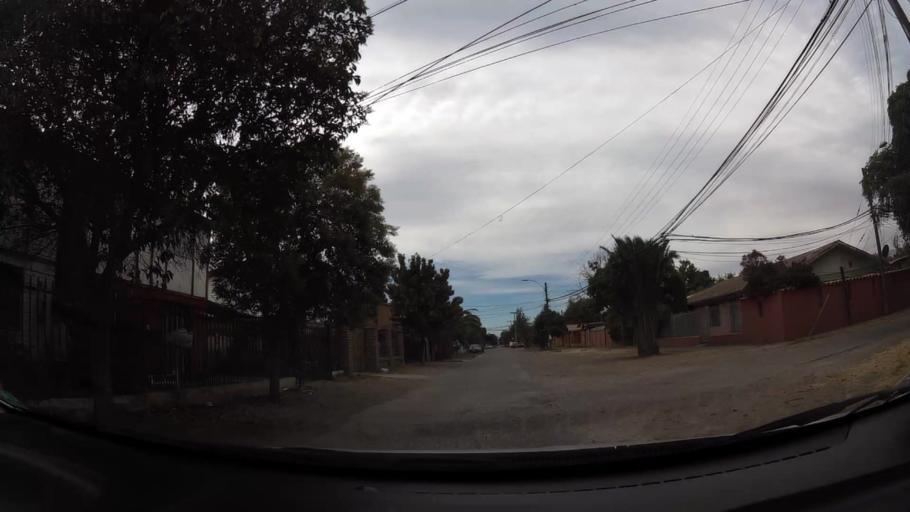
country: CL
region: O'Higgins
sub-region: Provincia de Cachapoal
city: Rancagua
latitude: -34.1503
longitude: -70.7338
